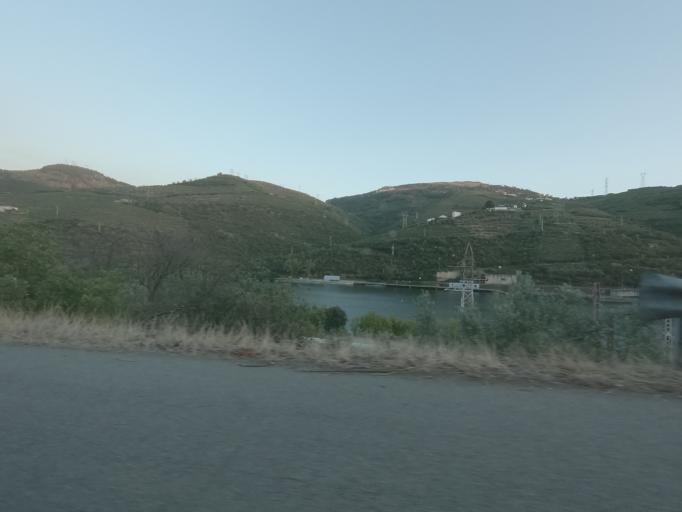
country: PT
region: Vila Real
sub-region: Peso da Regua
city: Peso da Regua
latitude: 41.1479
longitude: -7.7369
